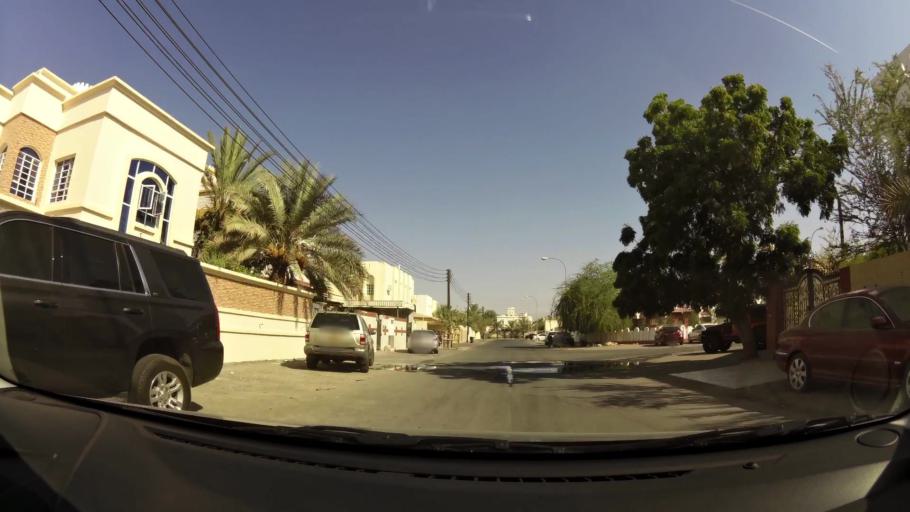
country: OM
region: Muhafazat Masqat
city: As Sib al Jadidah
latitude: 23.6303
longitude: 58.2065
